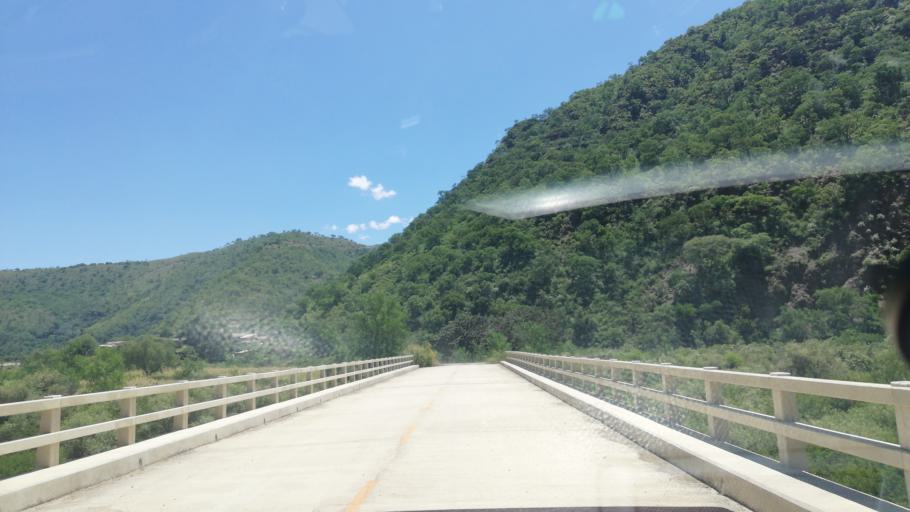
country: BO
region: Cochabamba
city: Mizque
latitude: -17.8186
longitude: -65.2946
